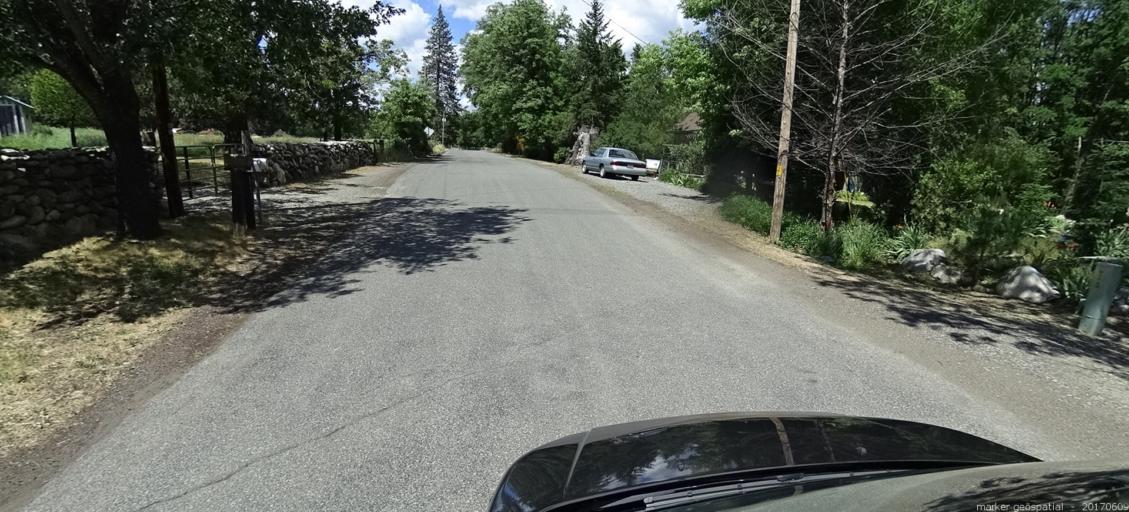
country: US
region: California
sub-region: Siskiyou County
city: Yreka
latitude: 41.4385
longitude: -122.9066
